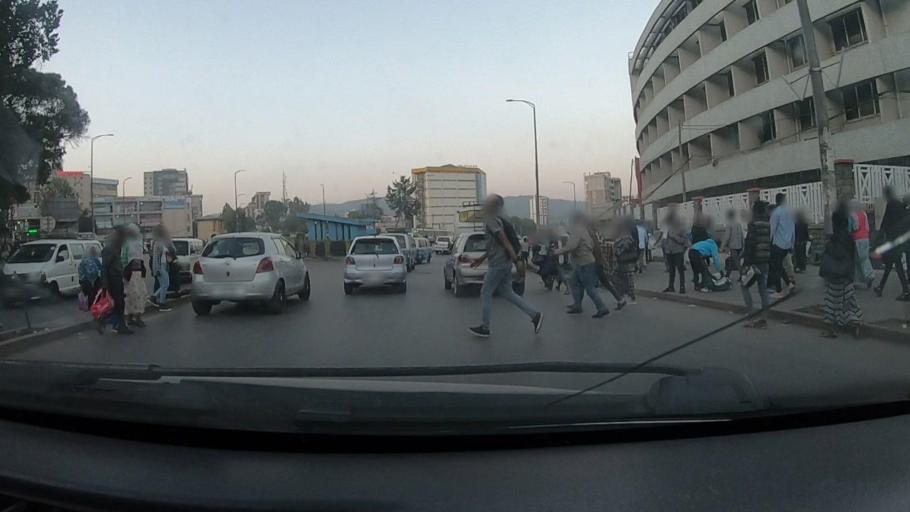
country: ET
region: Adis Abeba
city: Addis Ababa
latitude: 9.0370
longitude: 38.7524
